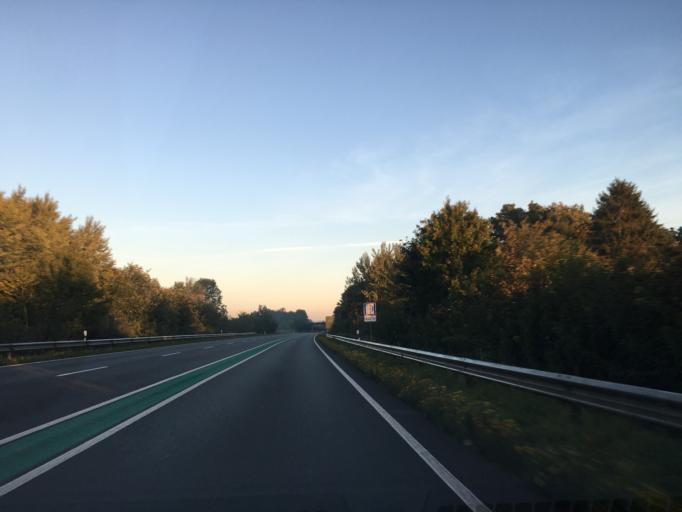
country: DE
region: North Rhine-Westphalia
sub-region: Regierungsbezirk Munster
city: Laer
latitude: 52.1053
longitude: 7.3833
